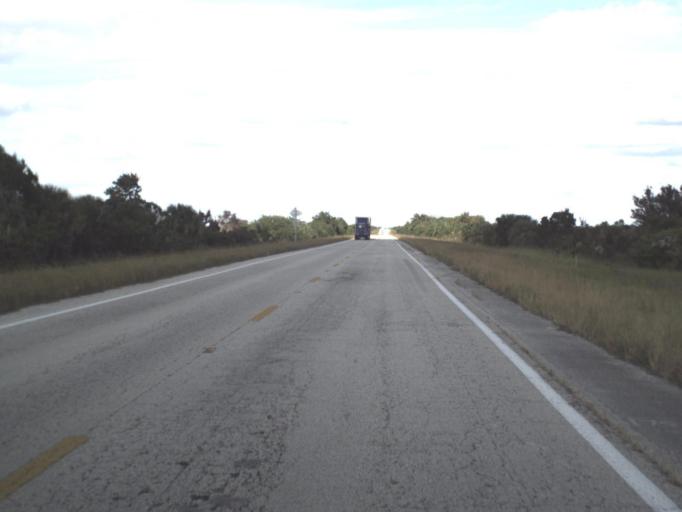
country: US
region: Florida
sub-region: Brevard County
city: Port Saint John
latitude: 28.4767
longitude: -80.8556
